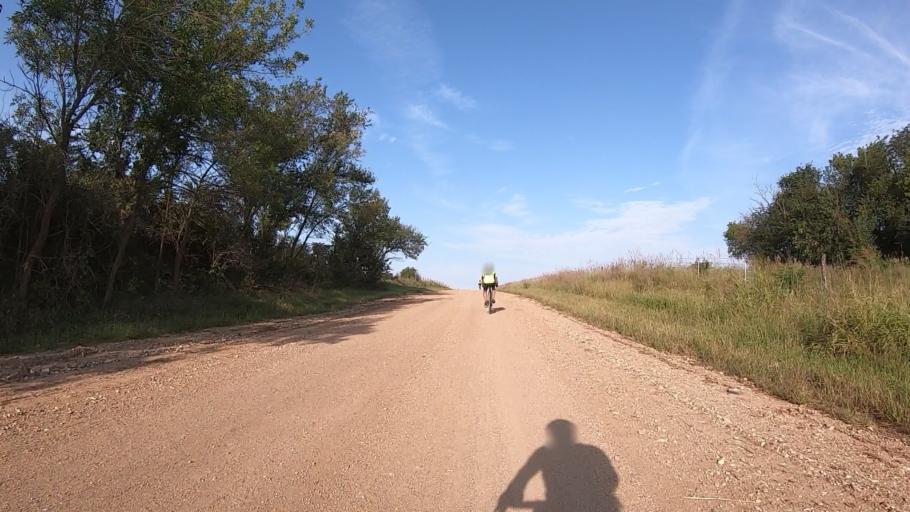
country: US
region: Kansas
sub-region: Marshall County
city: Blue Rapids
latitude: 39.6753
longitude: -96.7921
